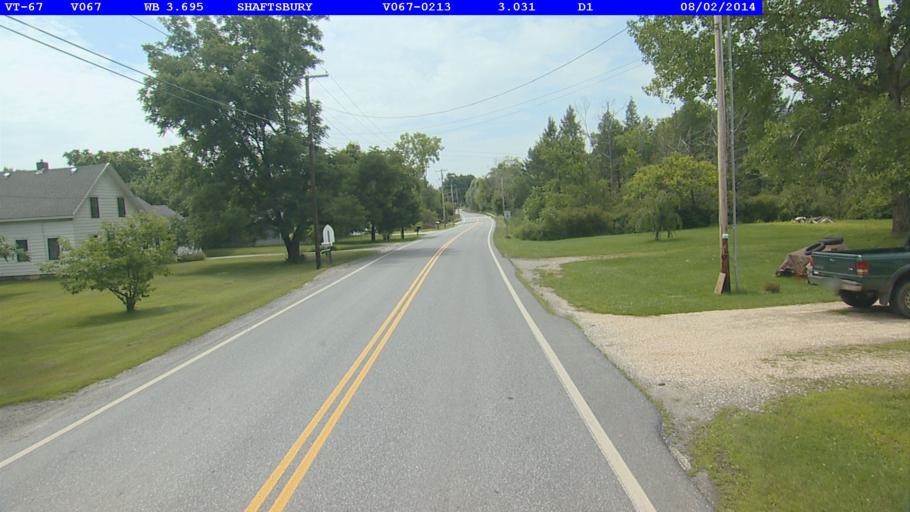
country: US
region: Vermont
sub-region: Bennington County
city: North Bennington
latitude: 42.9456
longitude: -73.2204
